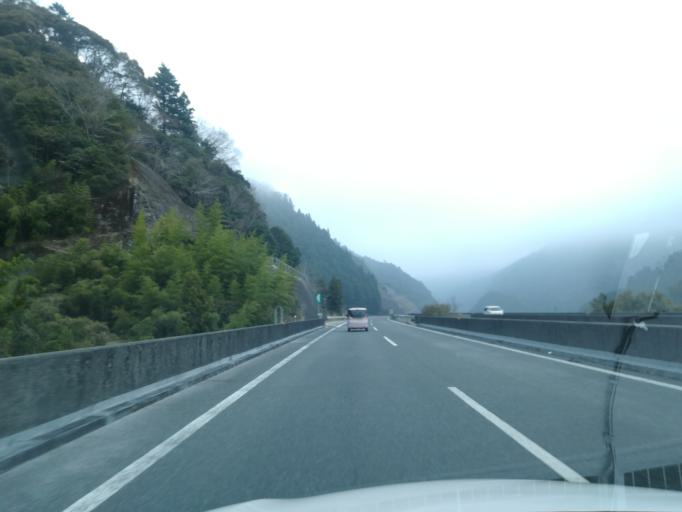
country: JP
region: Ehime
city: Kawanoecho
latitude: 33.7813
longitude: 133.6613
